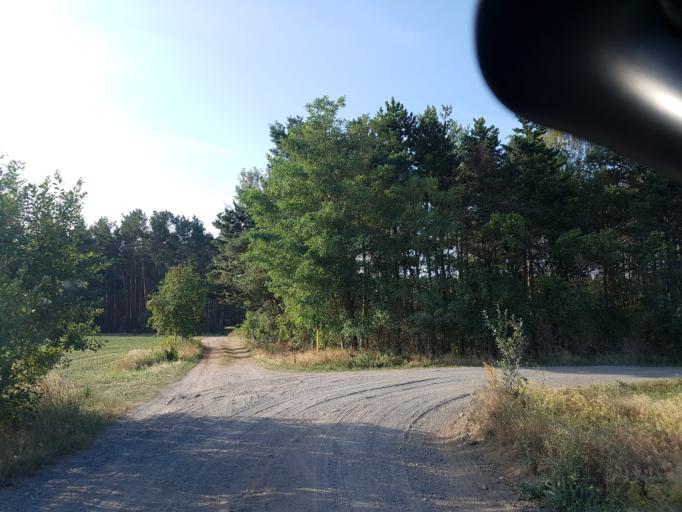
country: DE
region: Brandenburg
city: Niemegk
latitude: 52.0764
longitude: 12.7163
